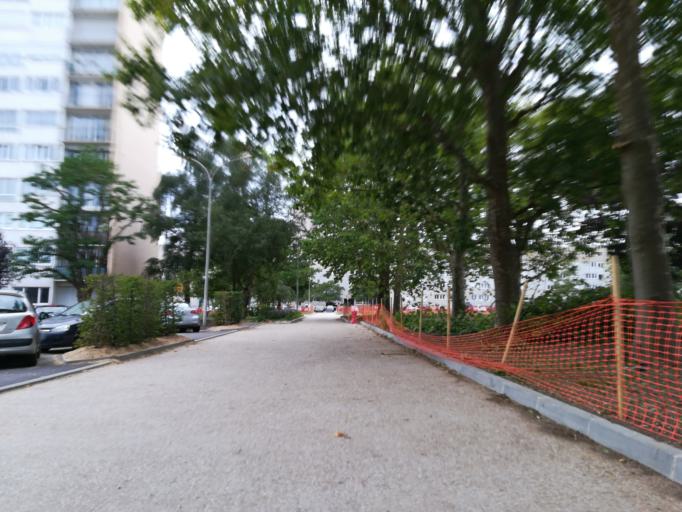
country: FR
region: Haute-Normandie
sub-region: Departement de la Seine-Maritime
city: Deville-les-Rouen
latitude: 49.4630
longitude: 1.0713
